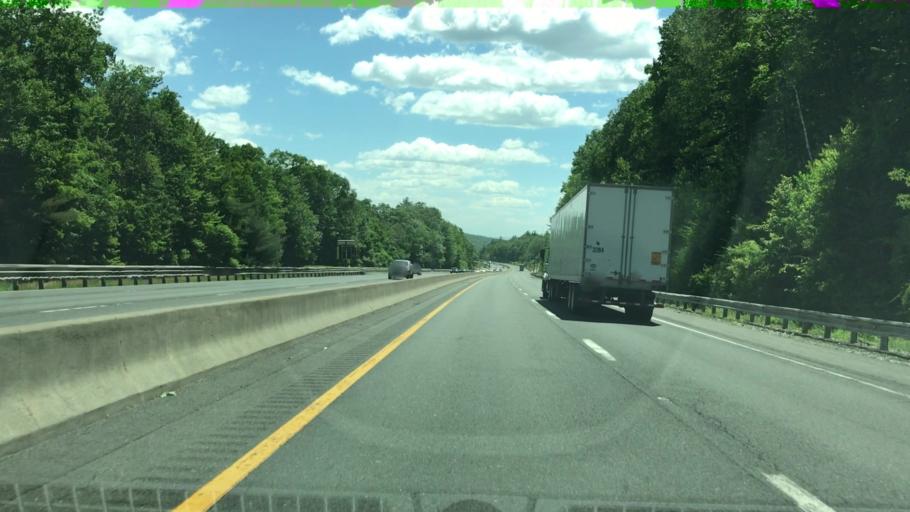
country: US
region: Massachusetts
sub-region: Hampden County
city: Westfield
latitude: 42.1604
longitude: -72.8272
